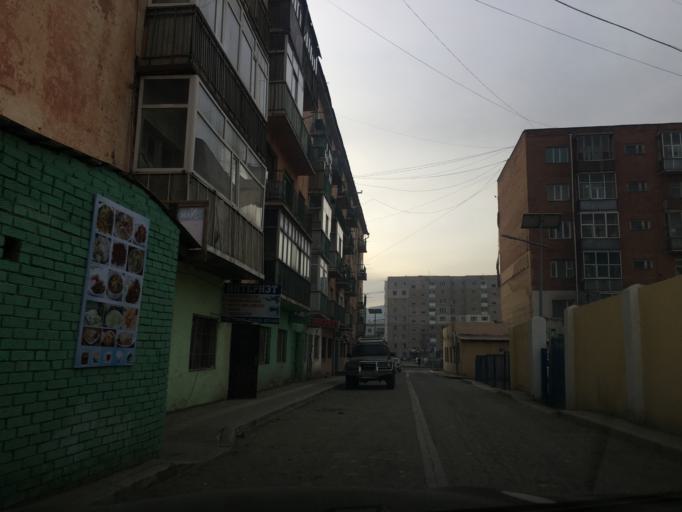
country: MN
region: Ulaanbaatar
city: Ulaanbaatar
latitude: 47.9157
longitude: 106.8877
